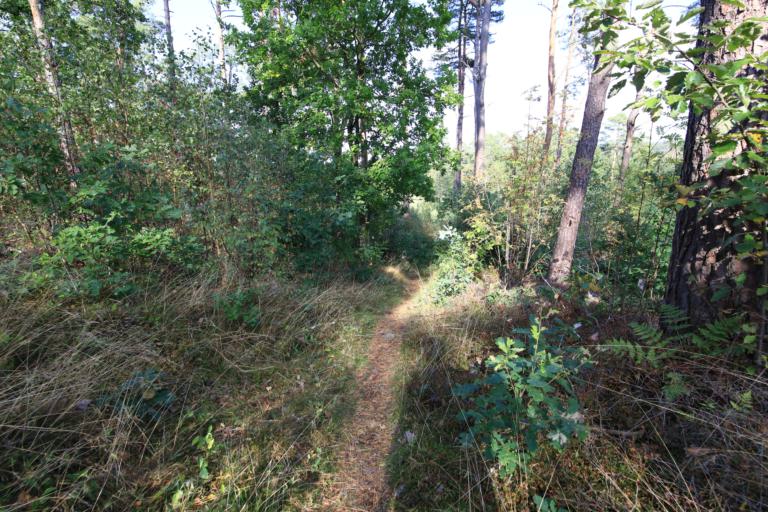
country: SE
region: Halland
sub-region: Varbergs Kommun
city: Varberg
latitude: 57.1777
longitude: 12.2193
